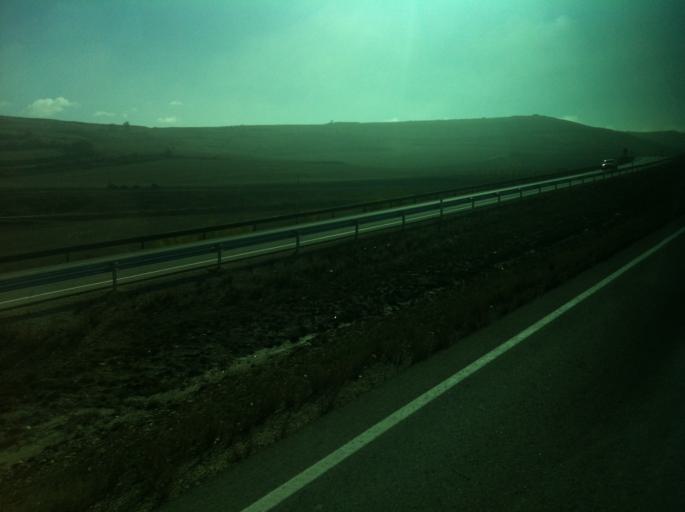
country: ES
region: Castille and Leon
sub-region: Provincia de Burgos
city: Rubena
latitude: 42.3857
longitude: -3.5821
